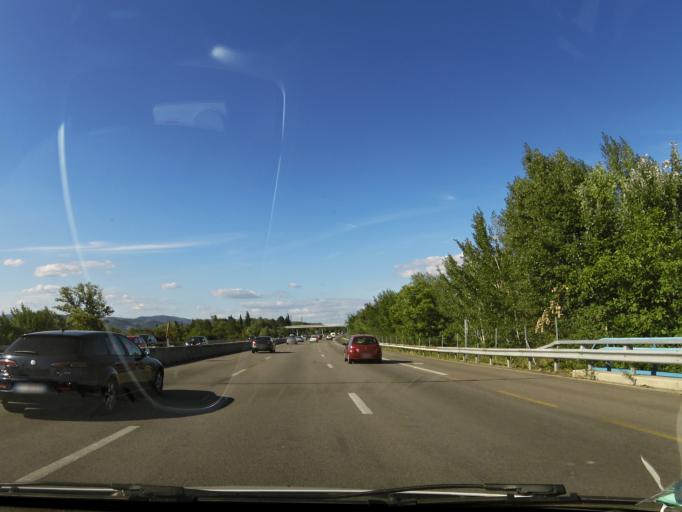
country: FR
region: Rhone-Alpes
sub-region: Departement de la Drome
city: Loriol-sur-Drome
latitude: 44.7463
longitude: 4.7892
